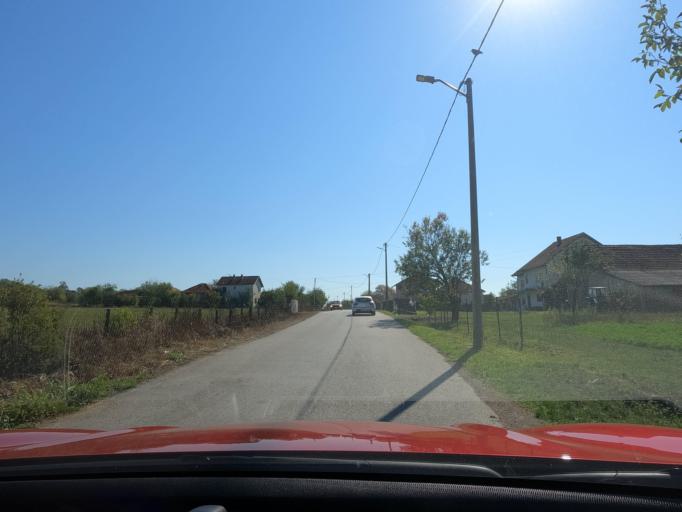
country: RS
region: Central Serbia
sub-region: Raski Okrug
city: Kraljevo
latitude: 43.7600
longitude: 20.6802
